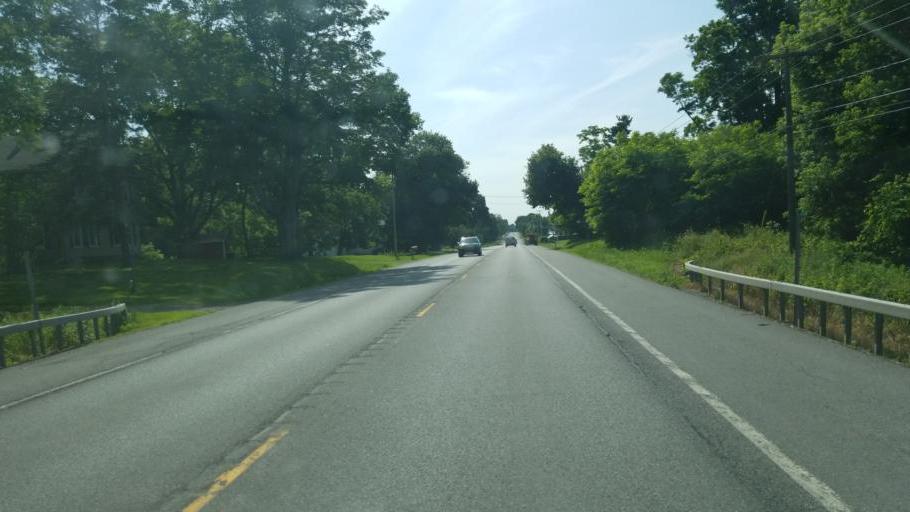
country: US
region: New York
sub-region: Monroe County
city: Honeoye Falls
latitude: 42.9039
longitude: -77.5165
